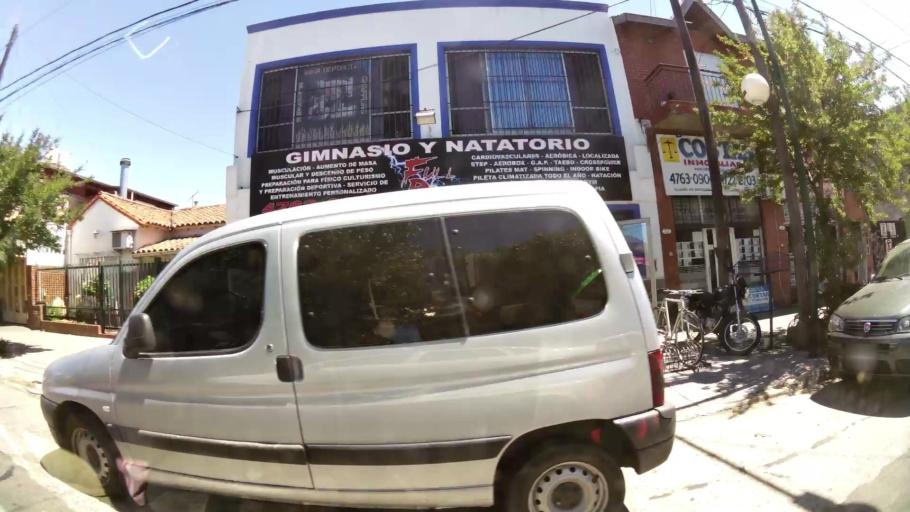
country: AR
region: Buenos Aires
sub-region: Partido de San Isidro
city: San Isidro
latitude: -34.5120
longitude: -58.5685
